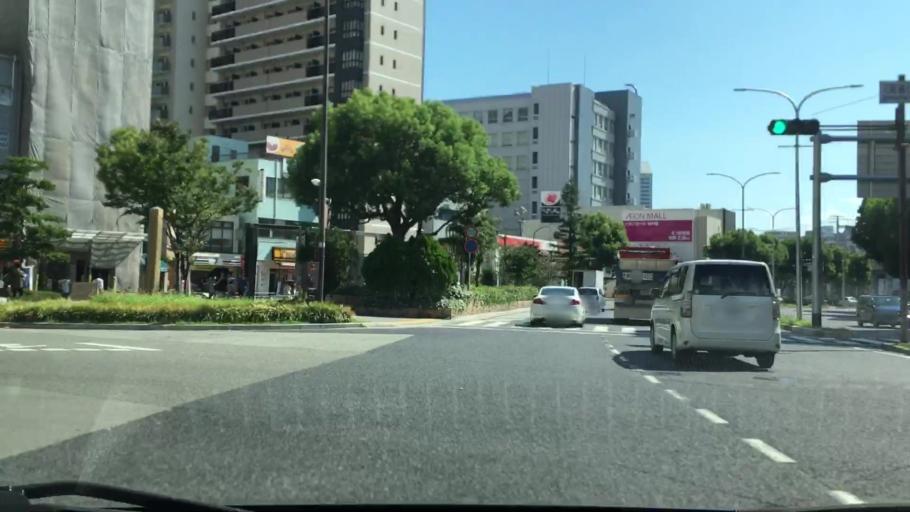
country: JP
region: Hyogo
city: Kobe
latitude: 34.6832
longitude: 135.1796
